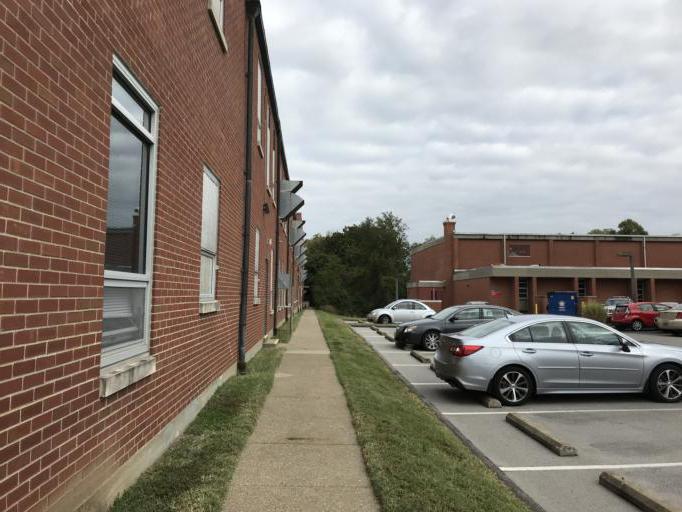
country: US
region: Indiana
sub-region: Clark County
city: Jeffersonville
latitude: 38.2573
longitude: -85.7140
